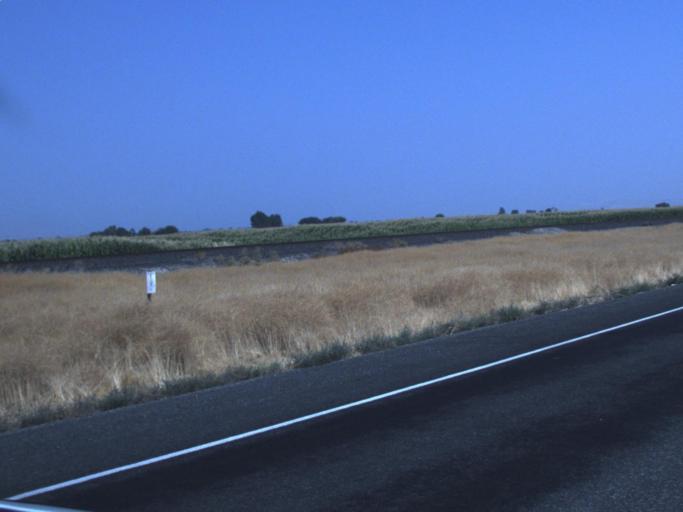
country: US
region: Washington
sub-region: Yakima County
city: Mabton
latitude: 46.2042
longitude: -119.9694
